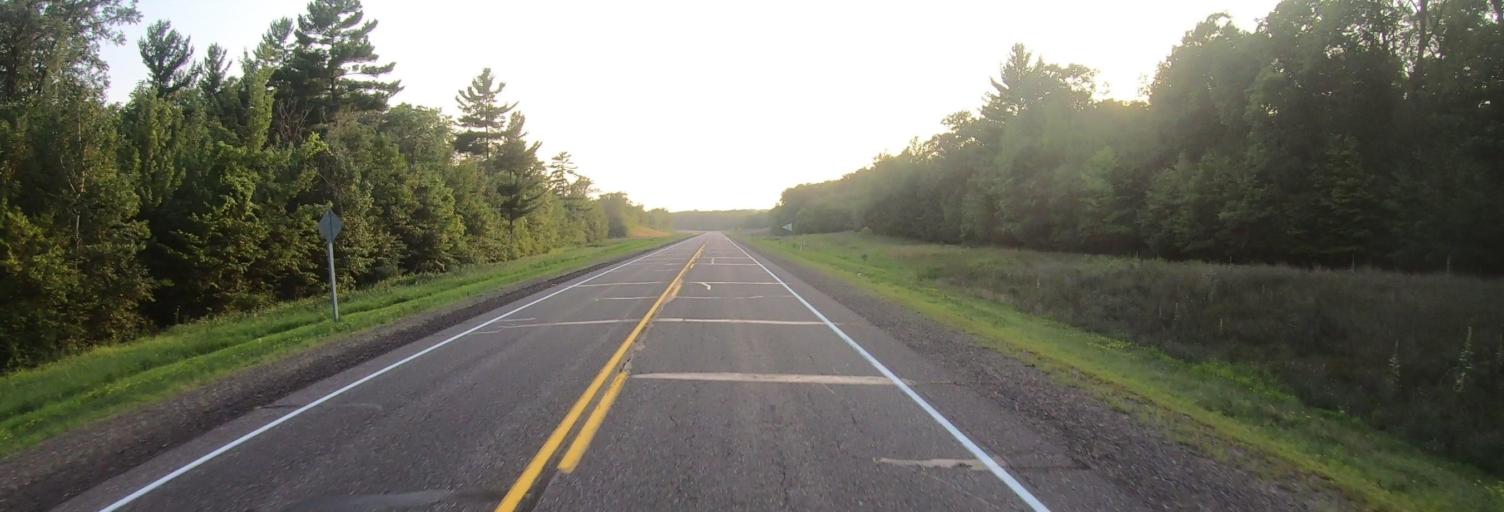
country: US
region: Wisconsin
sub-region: Burnett County
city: Siren
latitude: 45.7766
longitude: -92.4394
